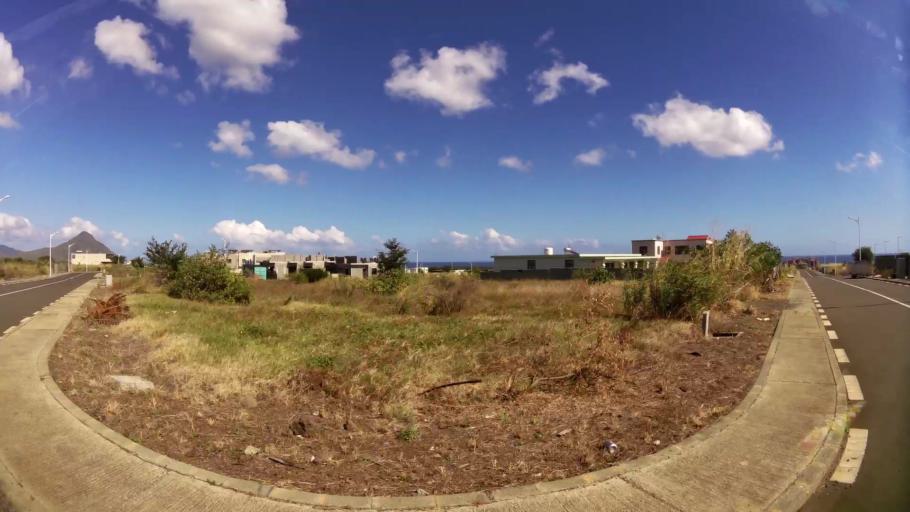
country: MU
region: Black River
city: Flic en Flac
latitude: -20.2780
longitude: 57.3854
